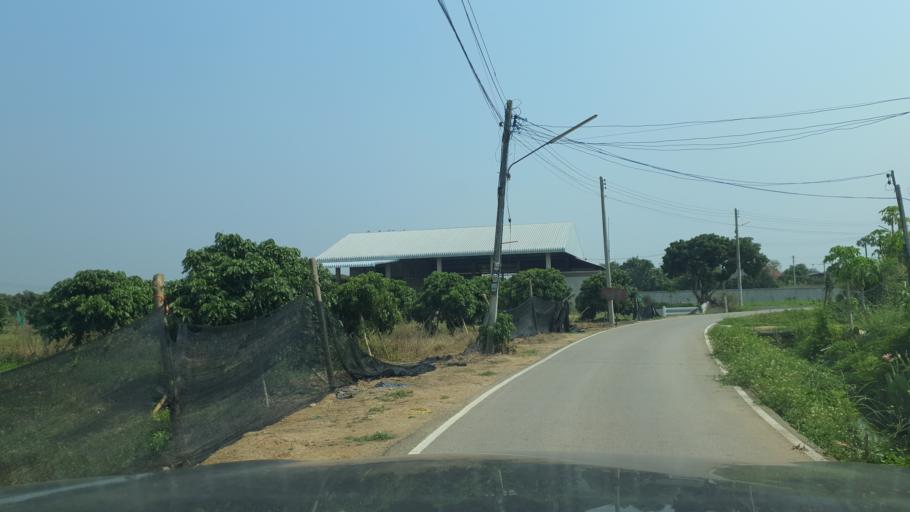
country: TH
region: Lamphun
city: Lamphun
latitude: 18.6533
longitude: 98.9880
